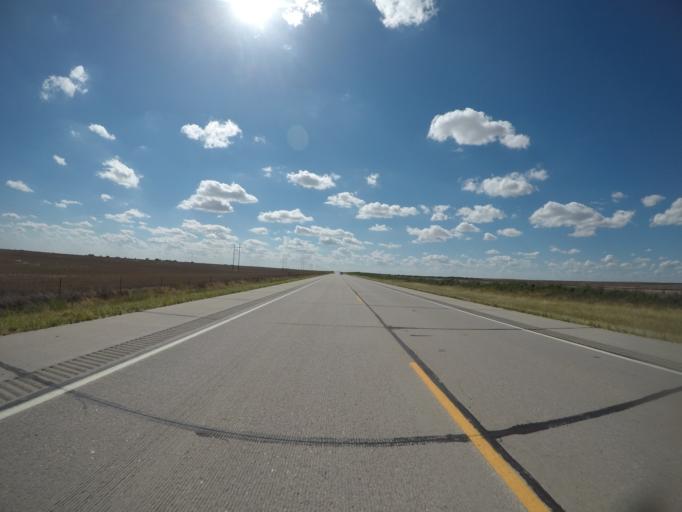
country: US
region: Colorado
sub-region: Phillips County
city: Holyoke
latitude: 40.5957
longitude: -102.3724
